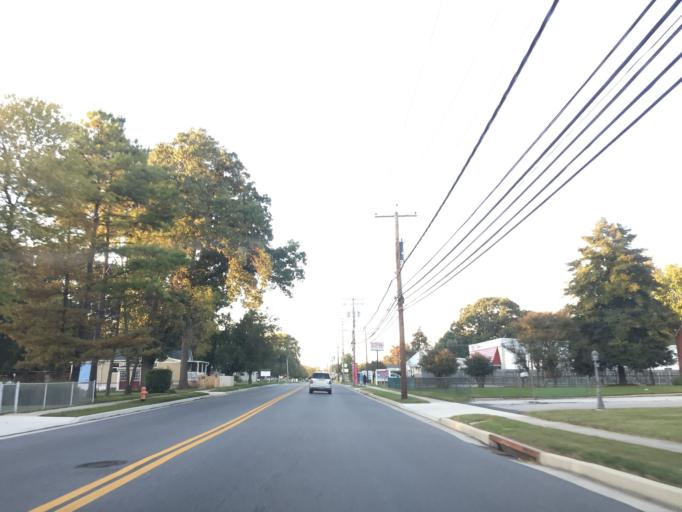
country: US
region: Maryland
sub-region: Baltimore County
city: Essex
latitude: 39.2992
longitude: -76.4616
